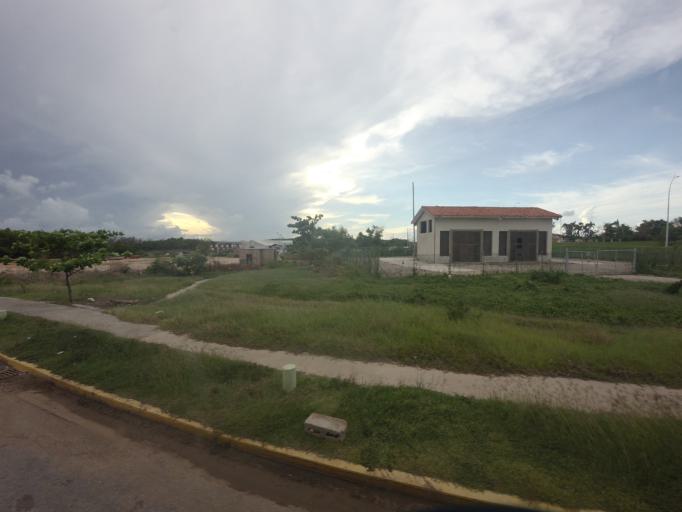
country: CU
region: Matanzas
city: Varadero
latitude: 23.1962
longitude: -81.1304
